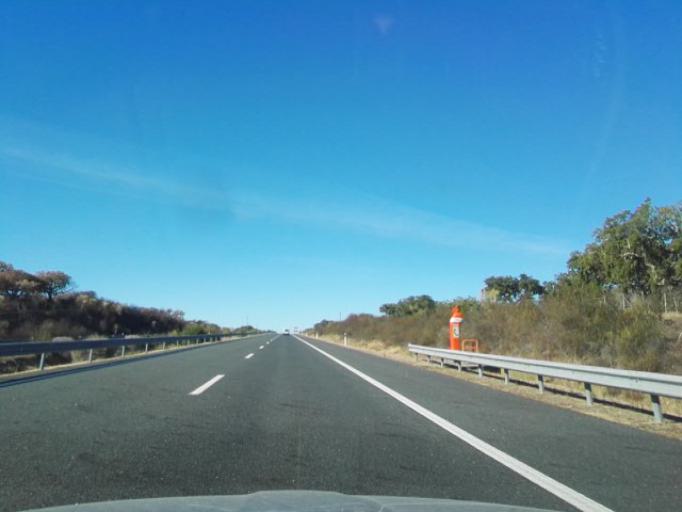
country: PT
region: Evora
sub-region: Estremoz
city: Estremoz
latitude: 38.7359
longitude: -7.7600
